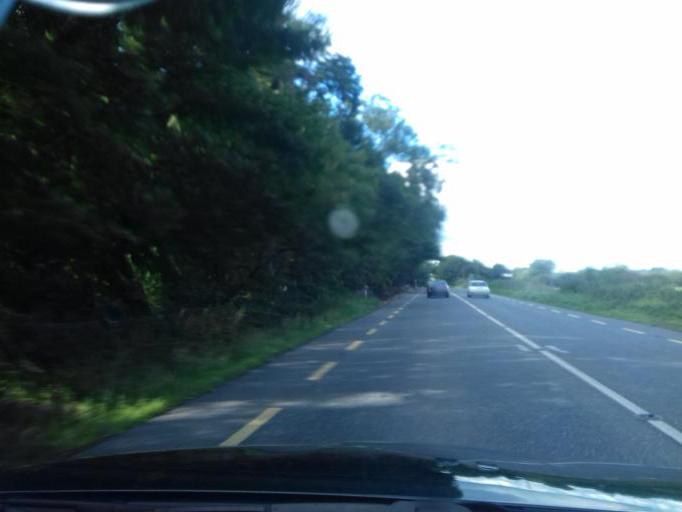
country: IE
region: Leinster
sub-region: Uibh Fhaili
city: Tullamore
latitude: 53.3180
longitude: -7.5110
